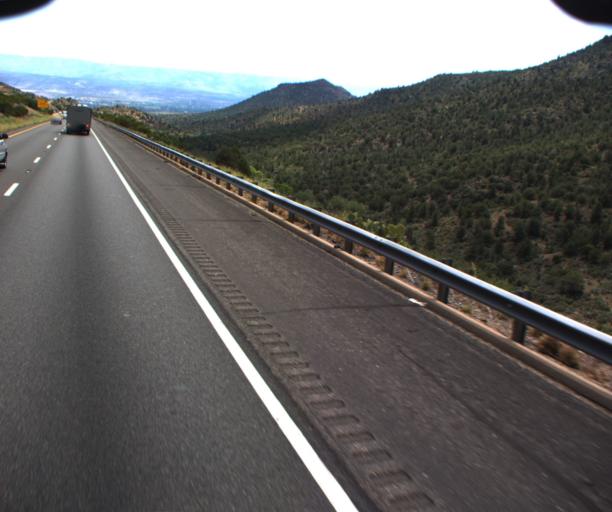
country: US
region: Arizona
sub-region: Yavapai County
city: Camp Verde
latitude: 34.5348
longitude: -111.9355
